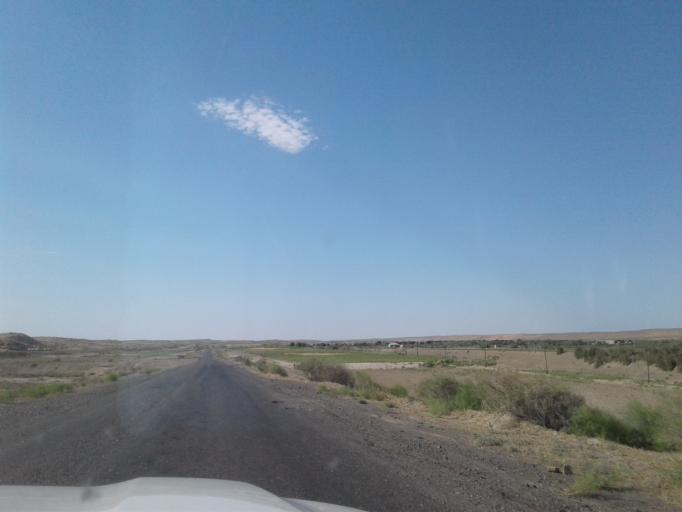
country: TM
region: Mary
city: Yoloeten
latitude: 36.6262
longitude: 62.4806
